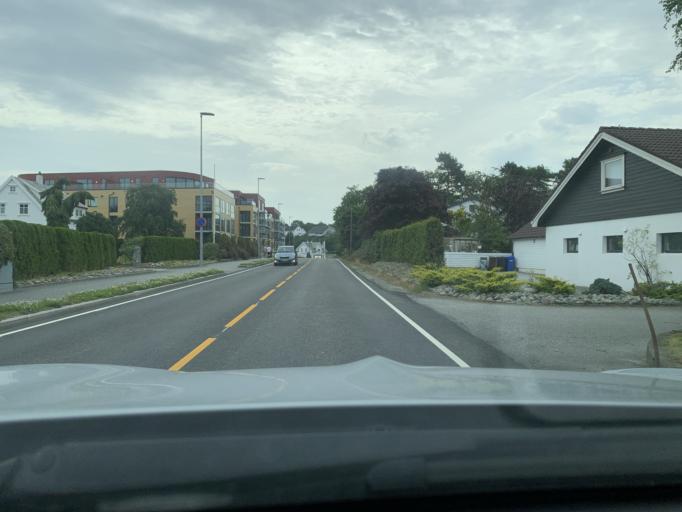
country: NO
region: Rogaland
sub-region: Sandnes
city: Sandnes
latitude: 58.7804
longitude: 5.7192
